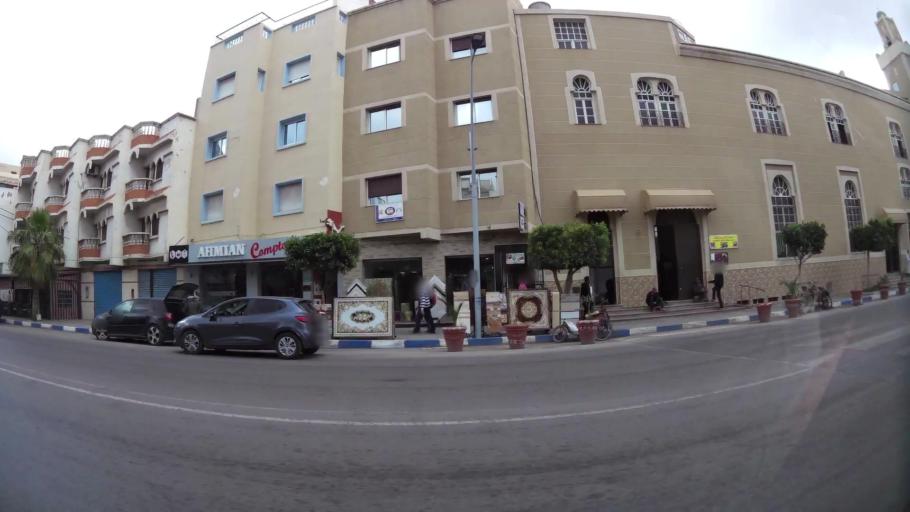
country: MA
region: Oriental
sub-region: Nador
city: Nador
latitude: 35.1654
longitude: -2.9320
